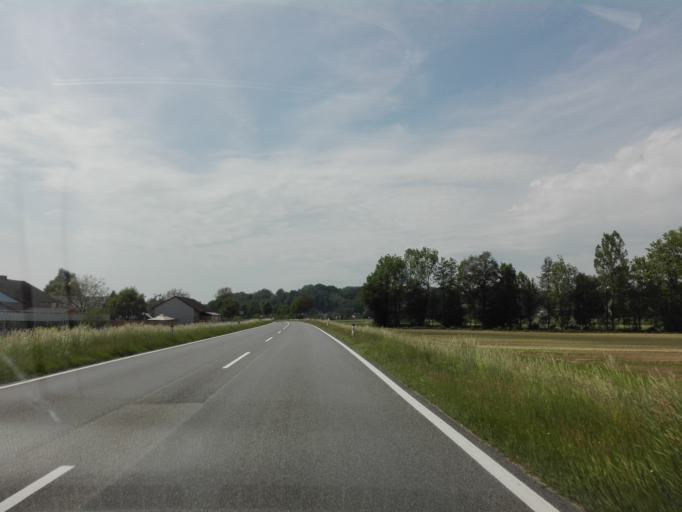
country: AT
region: Upper Austria
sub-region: Politischer Bezirk Perg
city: Bad Kreuzen
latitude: 48.2196
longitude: 14.7354
